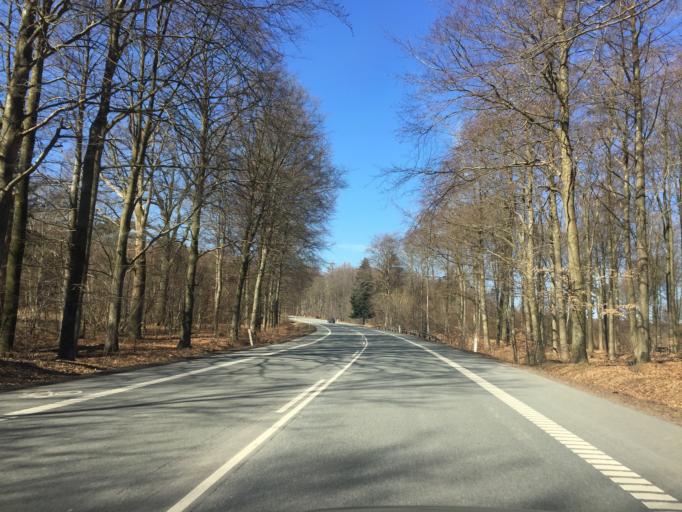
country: DK
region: Capital Region
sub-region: Fredensborg Kommune
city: Humlebaek
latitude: 56.0046
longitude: 12.4773
